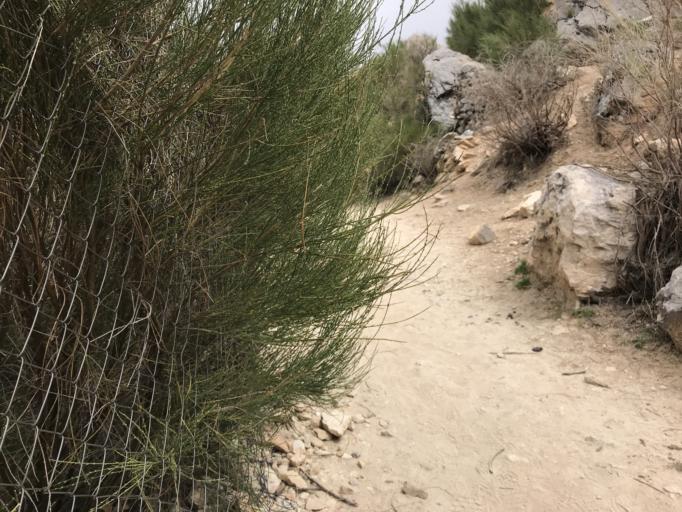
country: ES
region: Andalusia
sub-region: Provincia de Granada
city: Castril
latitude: 37.8949
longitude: -2.7477
